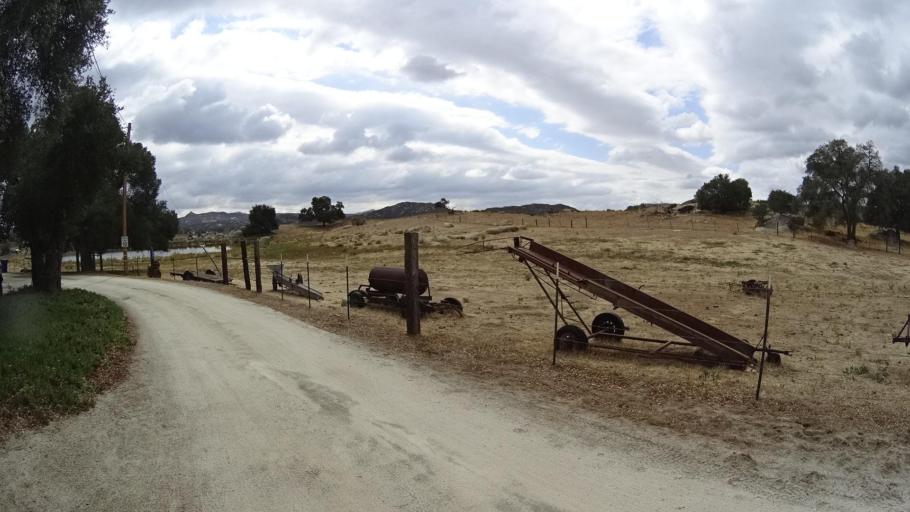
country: US
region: California
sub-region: San Diego County
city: Campo
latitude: 32.6266
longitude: -116.4708
